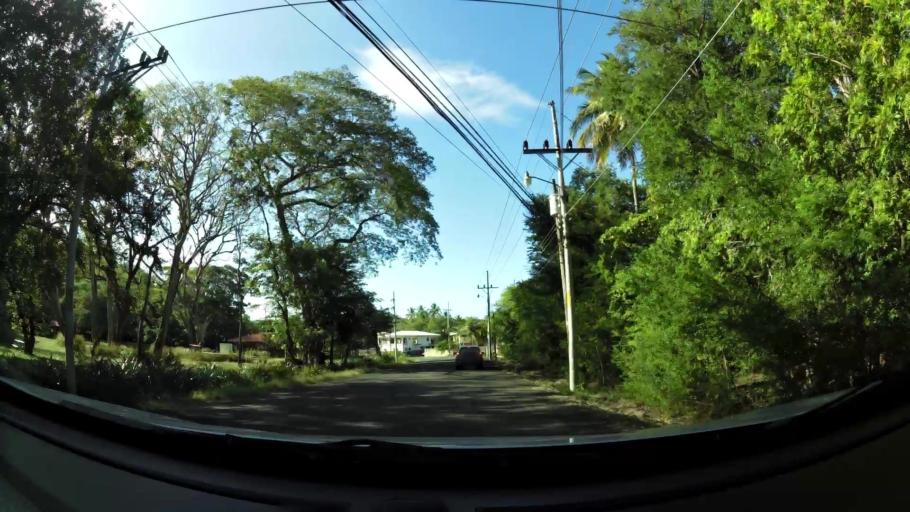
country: CR
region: Guanacaste
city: Sardinal
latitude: 10.5862
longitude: -85.6590
